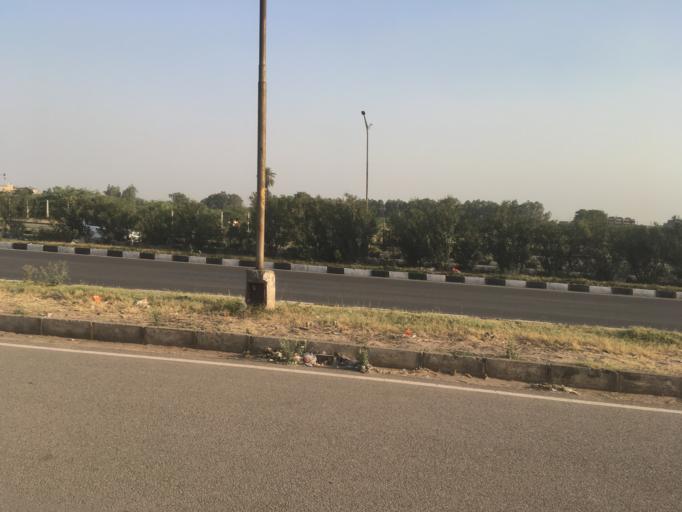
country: IN
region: Chandigarh
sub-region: Chandigarh
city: Chandigarh
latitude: 30.6895
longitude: 76.8214
